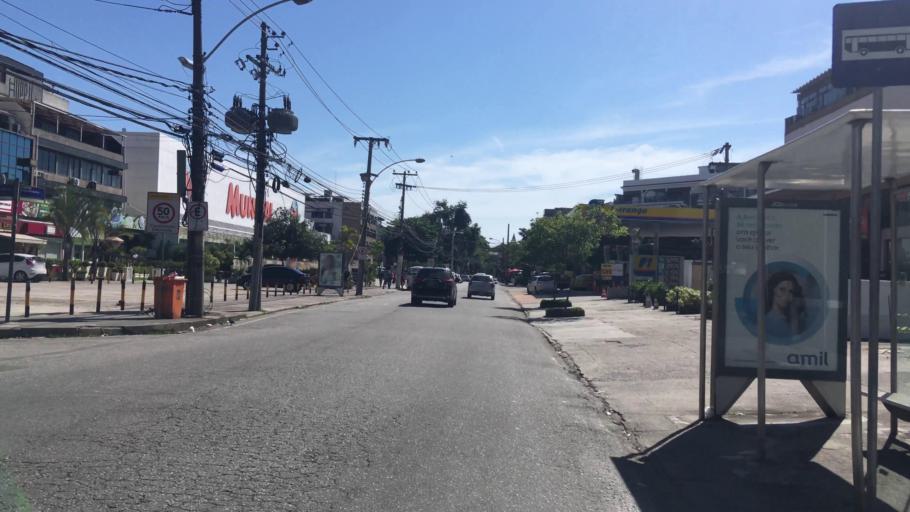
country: BR
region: Rio de Janeiro
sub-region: Rio De Janeiro
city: Rio de Janeiro
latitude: -23.0085
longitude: -43.3055
